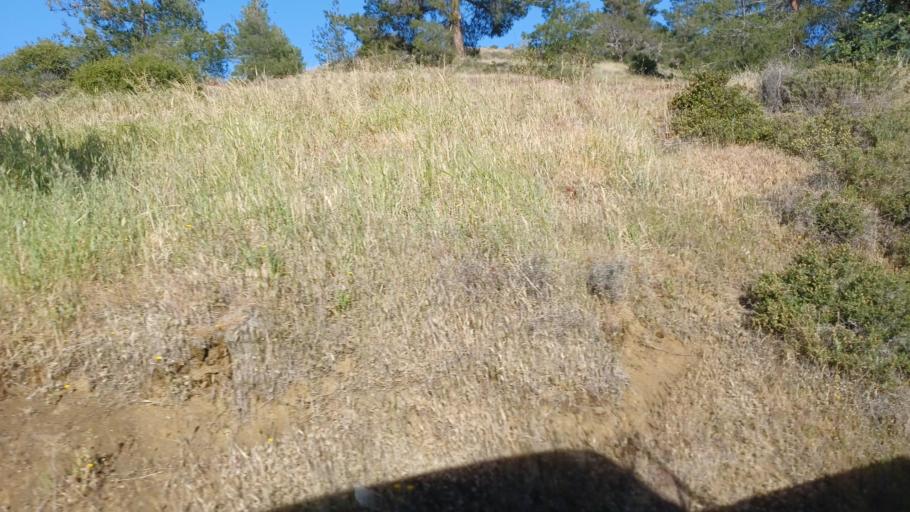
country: CY
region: Lefkosia
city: Peristerona
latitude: 35.0267
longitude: 33.0539
